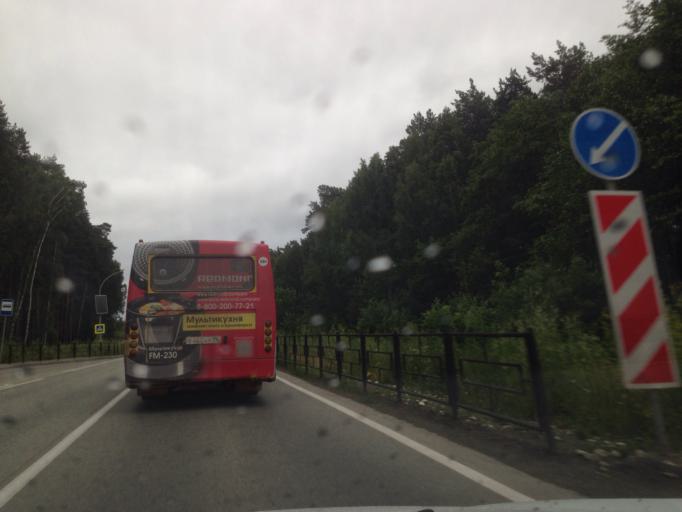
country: RU
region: Sverdlovsk
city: Istok
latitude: 56.8448
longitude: 60.7235
